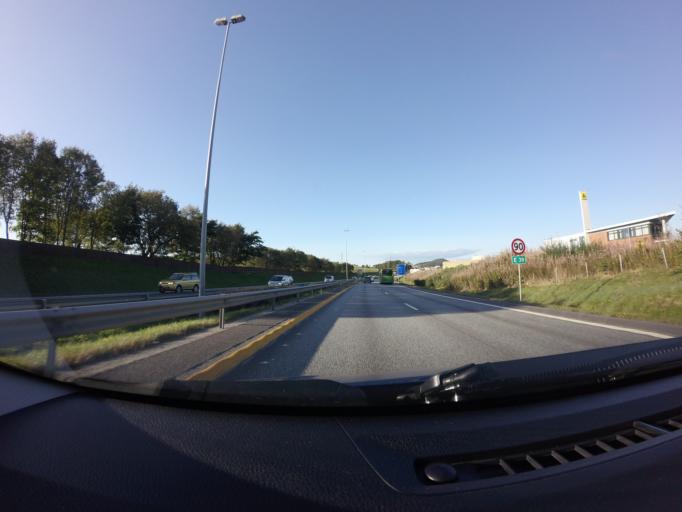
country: NO
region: Rogaland
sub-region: Sandnes
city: Sandnes
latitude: 58.8780
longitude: 5.7184
